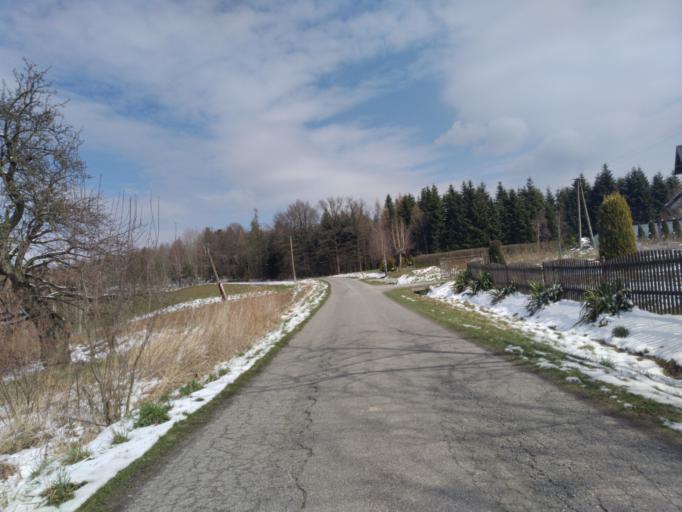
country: PL
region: Subcarpathian Voivodeship
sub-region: Powiat ropczycko-sedziszowski
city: Ropczyce
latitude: 50.0081
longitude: 21.5953
